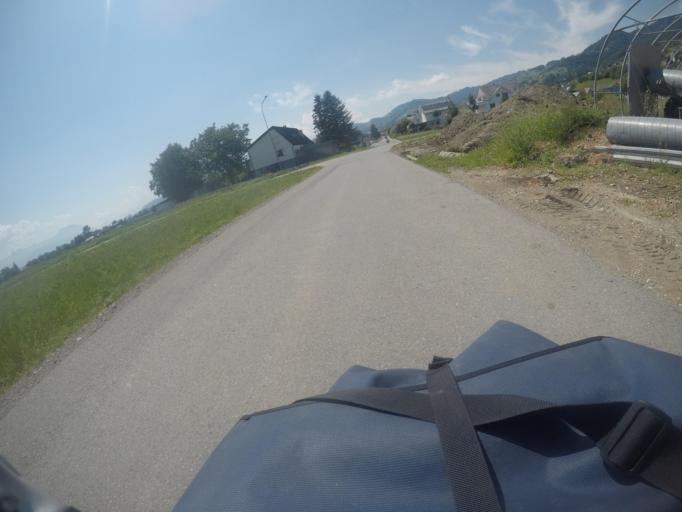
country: CH
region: Saint Gallen
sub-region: Wahlkreis Rheintal
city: Rebstein
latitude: 47.3940
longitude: 9.5771
